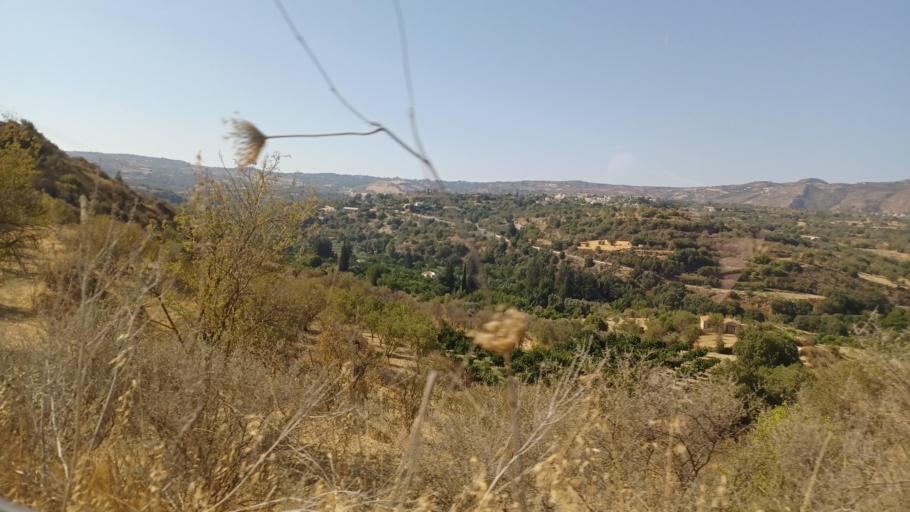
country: CY
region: Pafos
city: Tala
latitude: 34.9371
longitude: 32.4774
